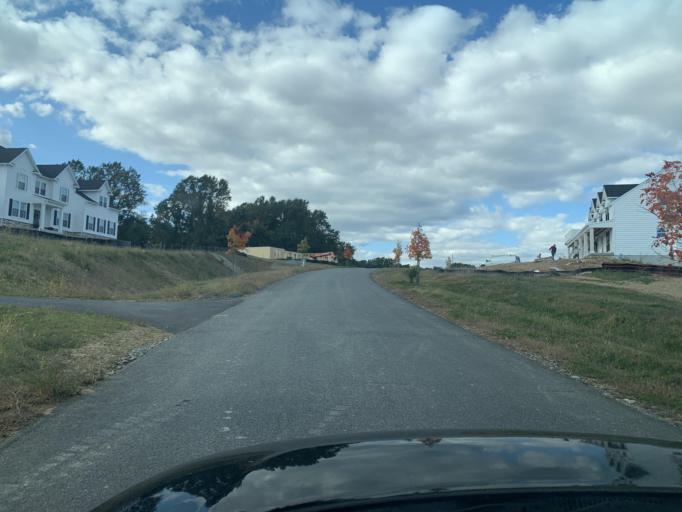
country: US
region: Maryland
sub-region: Harford County
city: Bel Air North
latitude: 39.5827
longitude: -76.4110
